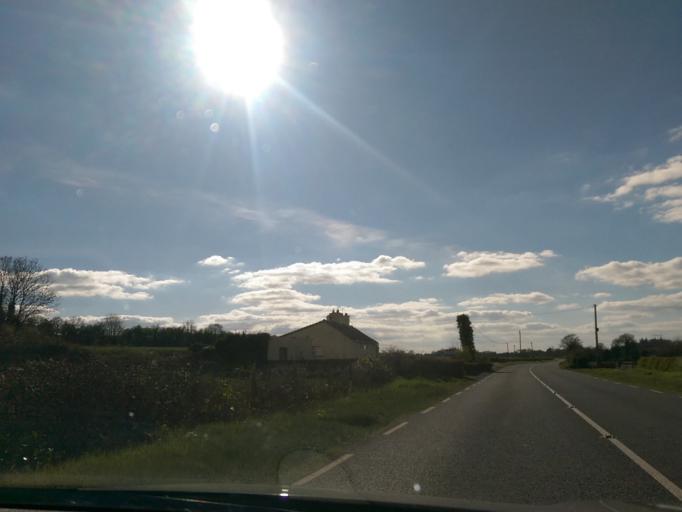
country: IE
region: Leinster
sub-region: Uibh Fhaili
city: Banagher
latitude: 53.1061
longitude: -8.0310
